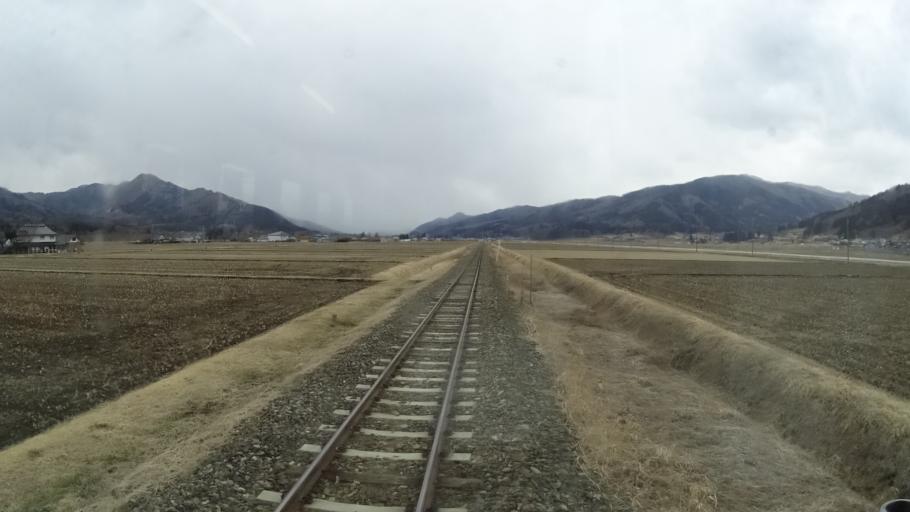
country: JP
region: Iwate
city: Tono
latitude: 39.3279
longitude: 141.4724
